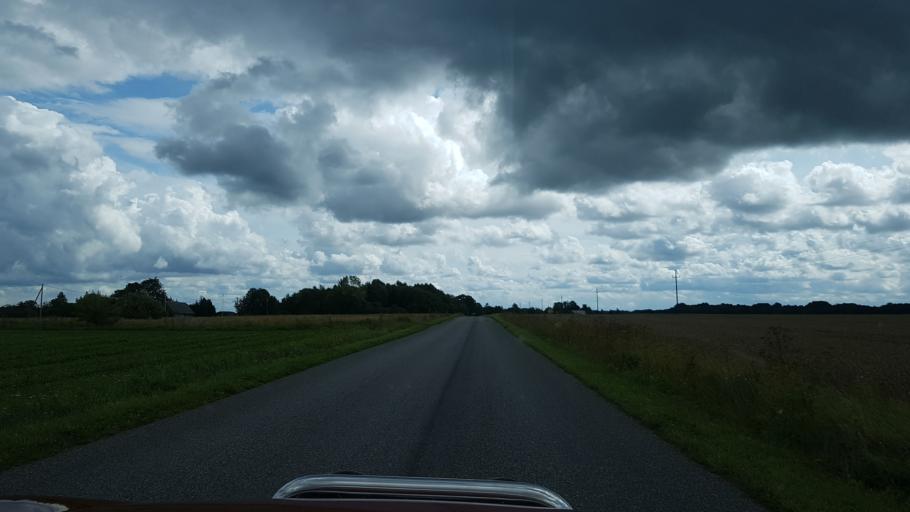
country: EE
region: Laeaene
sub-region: Lihula vald
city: Lihula
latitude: 58.7150
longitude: 23.9977
